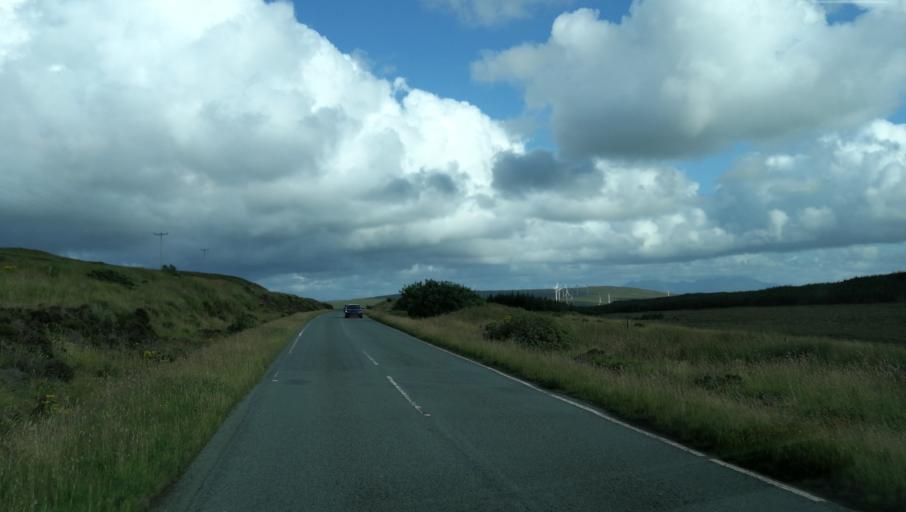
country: GB
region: Scotland
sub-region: Highland
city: Isle of Skye
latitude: 57.4671
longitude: -6.5154
